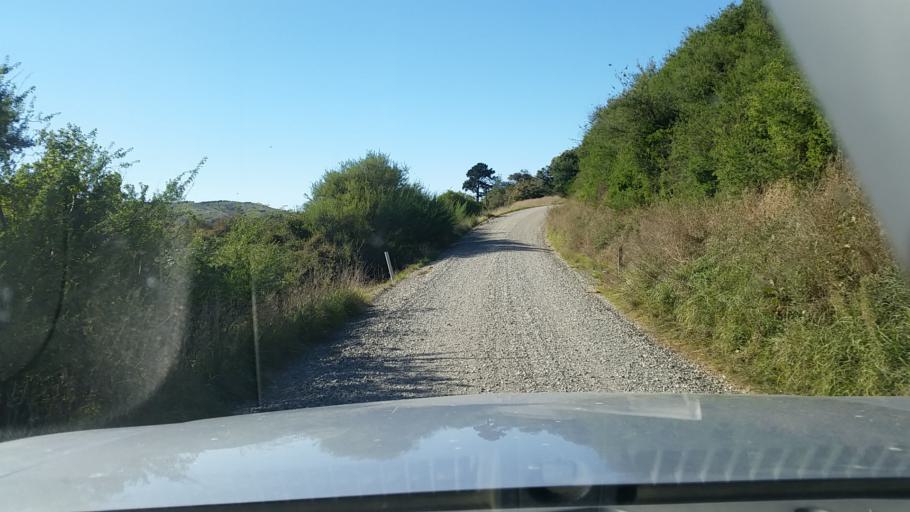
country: NZ
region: Marlborough
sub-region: Marlborough District
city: Blenheim
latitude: -41.6761
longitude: 174.1440
